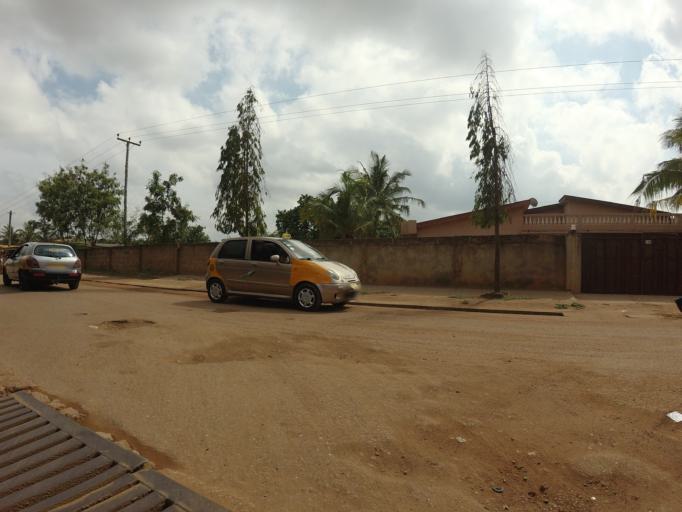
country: GH
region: Greater Accra
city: Nungua
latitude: 5.6131
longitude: -0.1010
